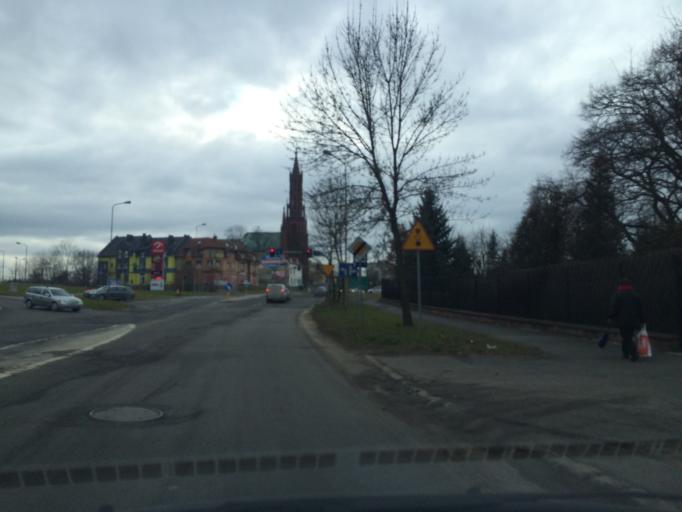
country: PL
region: Lower Silesian Voivodeship
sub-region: Powiat lubanski
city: Luban
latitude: 51.1244
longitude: 15.2933
